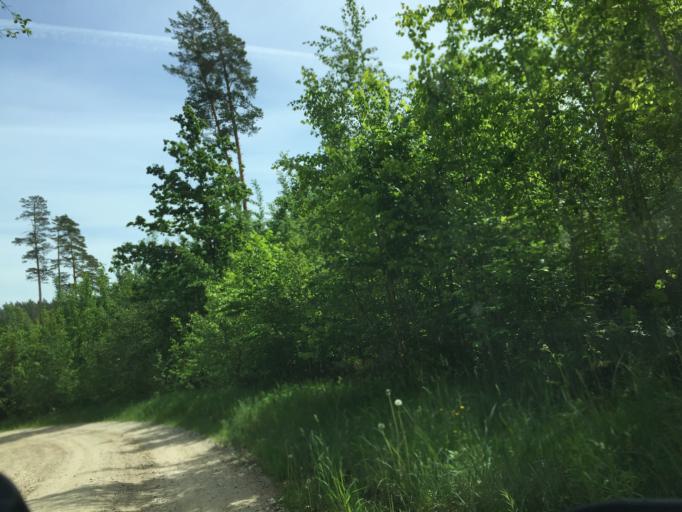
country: LV
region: Koceni
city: Koceni
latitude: 57.4755
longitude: 25.3743
